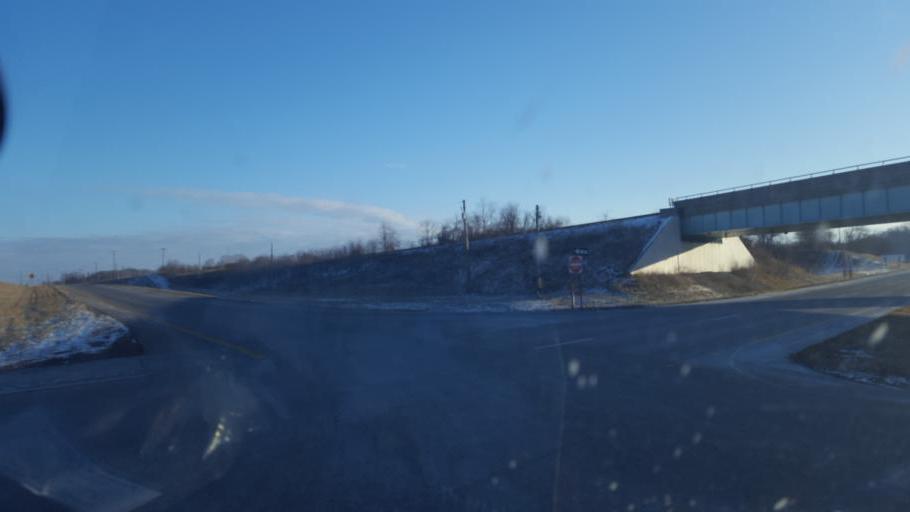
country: US
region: Ohio
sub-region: Pike County
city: Piketon
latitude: 39.0479
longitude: -83.0231
